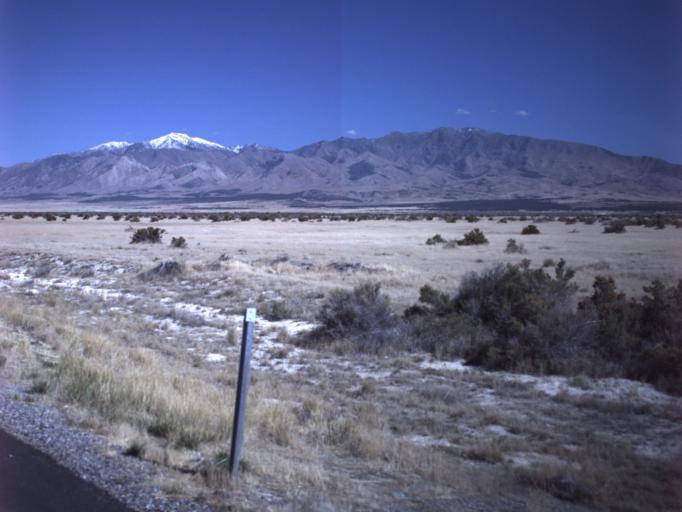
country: US
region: Utah
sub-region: Tooele County
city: Grantsville
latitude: 40.2713
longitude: -112.7413
